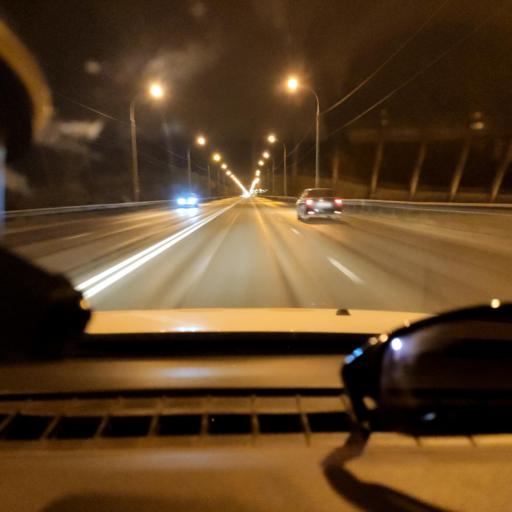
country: RU
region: Samara
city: Samara
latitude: 53.1525
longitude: 50.1879
